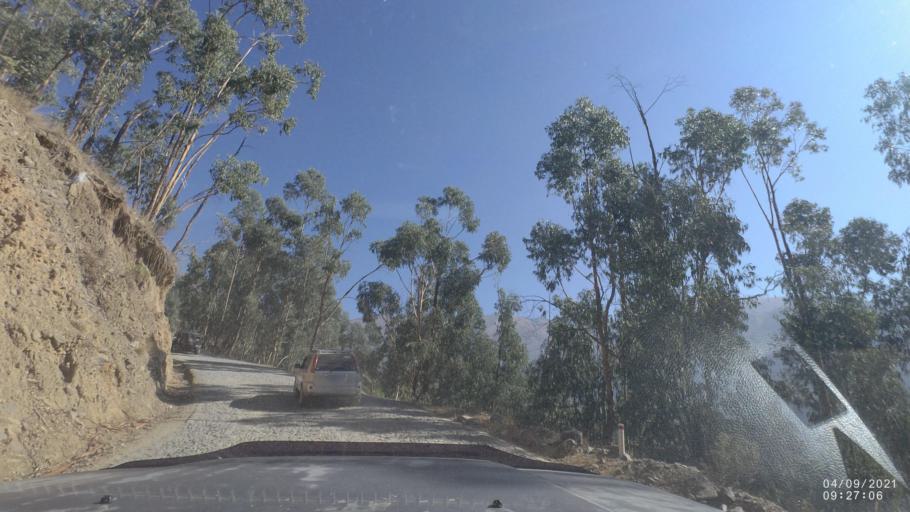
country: BO
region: Cochabamba
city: Sipe Sipe
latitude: -17.3580
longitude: -66.3716
